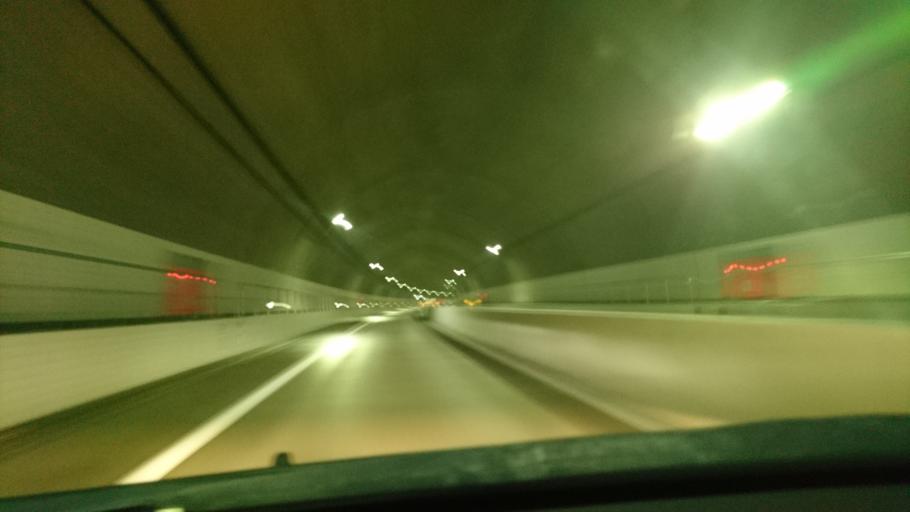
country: JP
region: Iwate
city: Miyako
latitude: 39.8117
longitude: 141.9578
